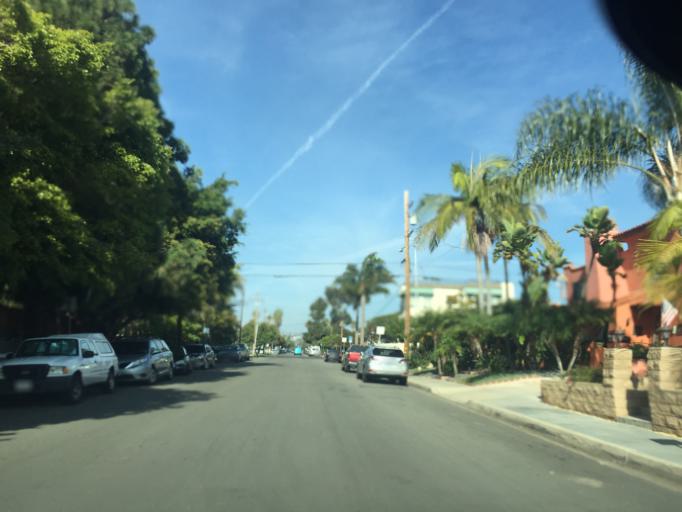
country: US
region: California
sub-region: San Diego County
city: La Jolla
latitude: 32.7931
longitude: -117.2486
